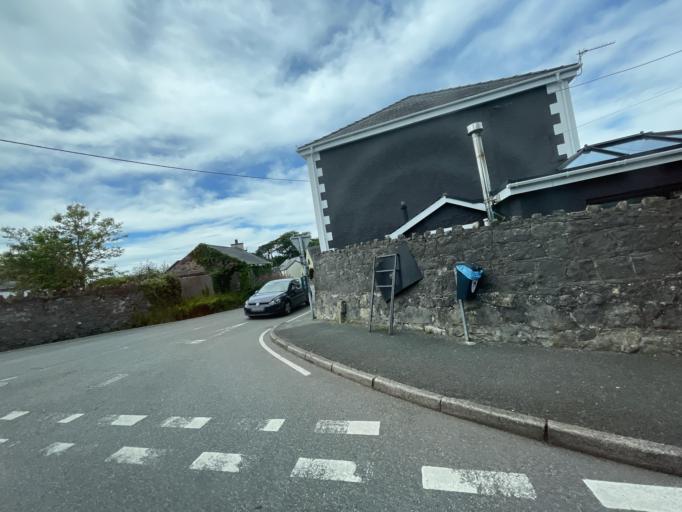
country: GB
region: Wales
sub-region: Anglesey
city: Gaerwen
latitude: 53.2103
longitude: -4.2547
